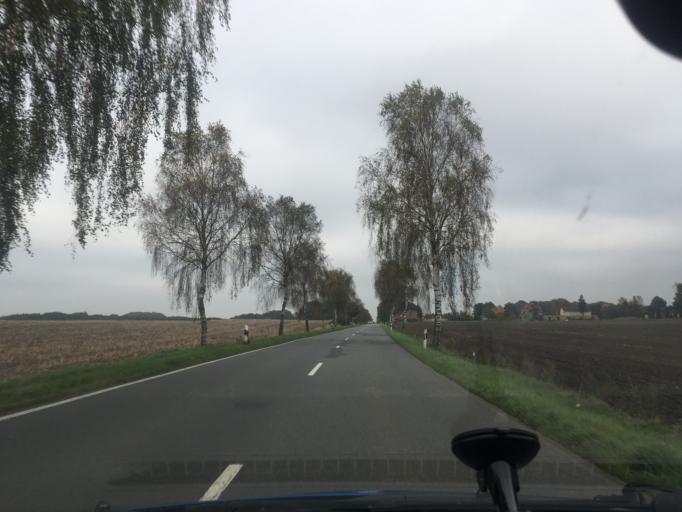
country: DE
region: Lower Saxony
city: Bispingen
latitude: 53.0764
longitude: 9.9788
